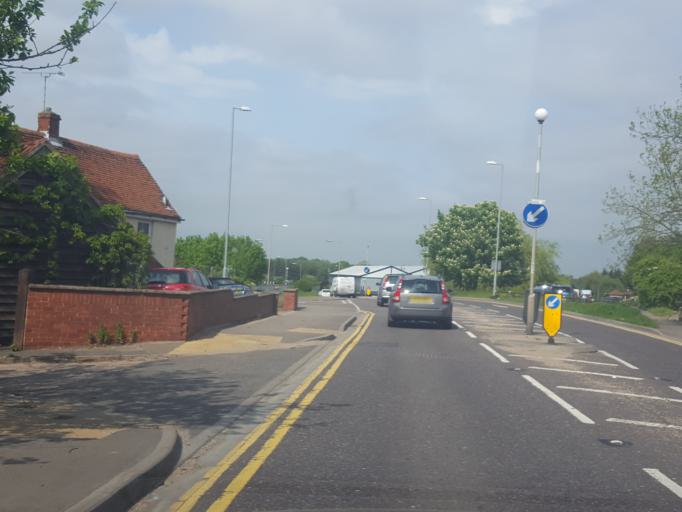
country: GB
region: England
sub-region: Essex
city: Colchester
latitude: 51.9182
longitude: 0.9322
